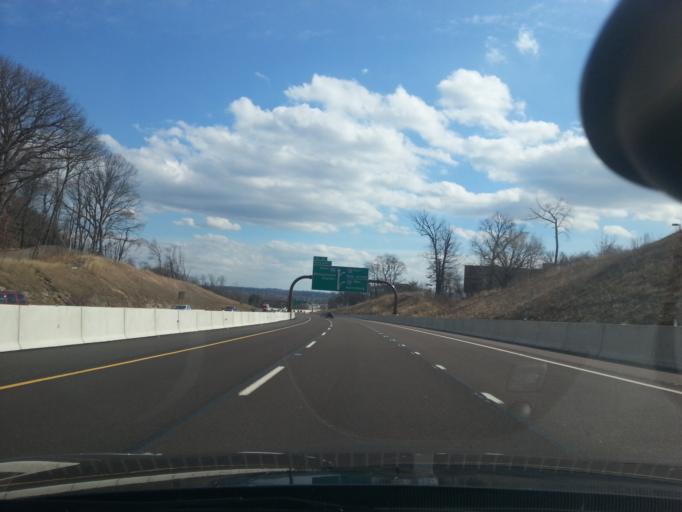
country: US
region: Pennsylvania
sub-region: Montgomery County
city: Plymouth Meeting
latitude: 40.1228
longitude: -75.2827
